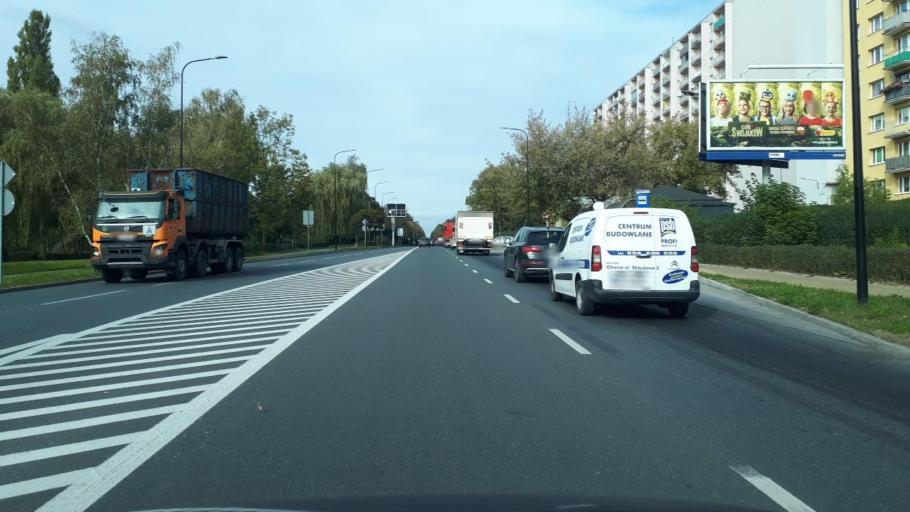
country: PL
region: Silesian Voivodeship
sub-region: Gliwice
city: Gliwice
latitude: 50.3175
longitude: 18.6656
